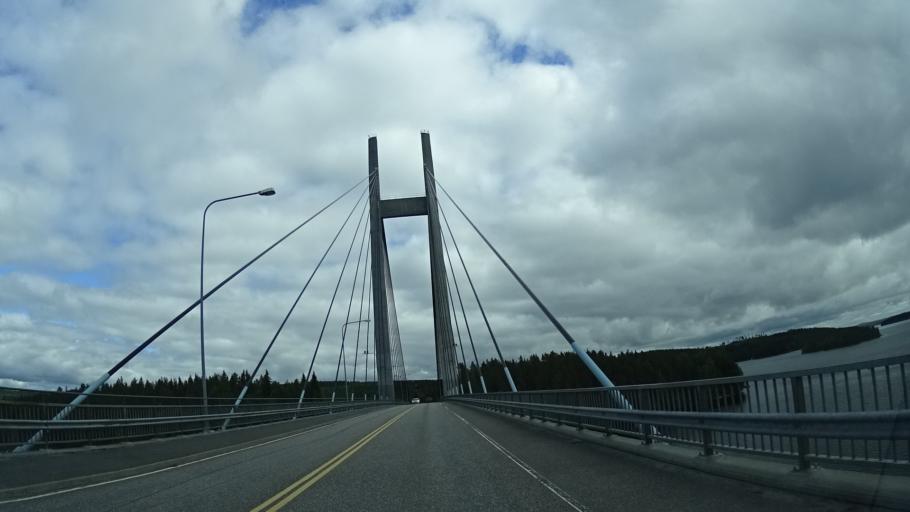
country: FI
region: Central Finland
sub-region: Jyvaeskylae
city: Korpilahti
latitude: 61.9981
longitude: 25.6760
